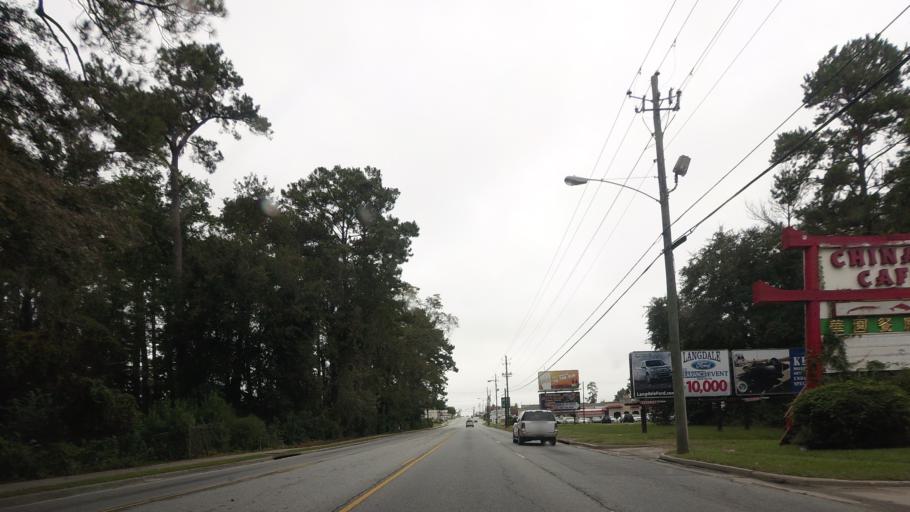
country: US
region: Georgia
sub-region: Lowndes County
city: Remerton
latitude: 30.8668
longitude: -83.2862
